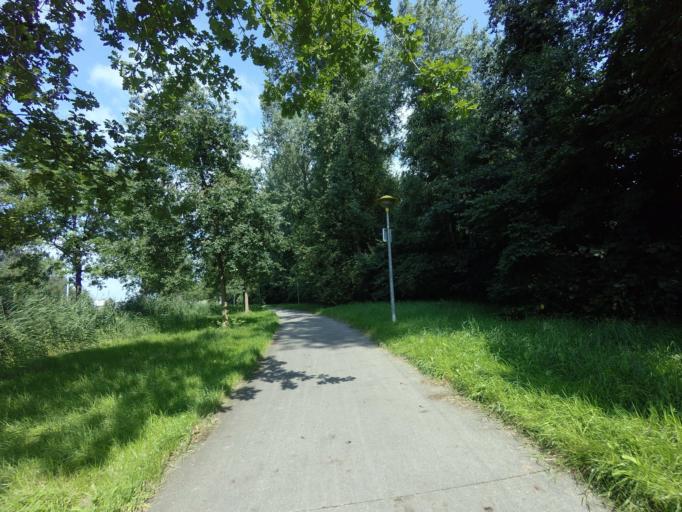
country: NL
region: Flevoland
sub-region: Gemeente Lelystad
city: Lelystad
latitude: 52.5292
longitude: 5.5191
